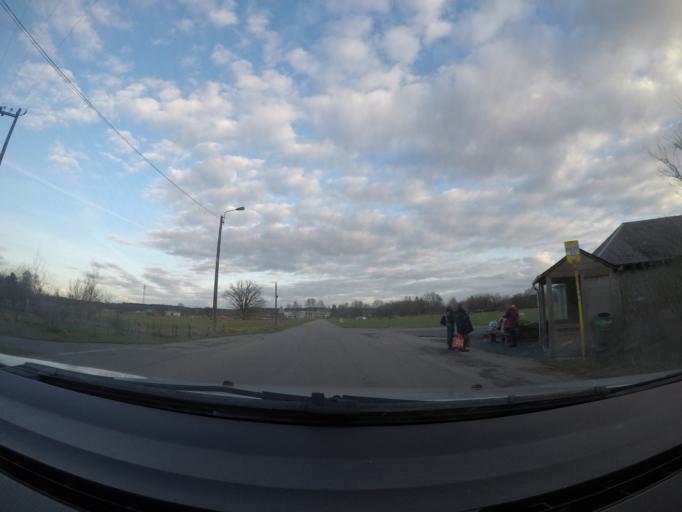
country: BE
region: Wallonia
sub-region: Province du Luxembourg
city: Etalle
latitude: 49.6696
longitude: 5.5674
